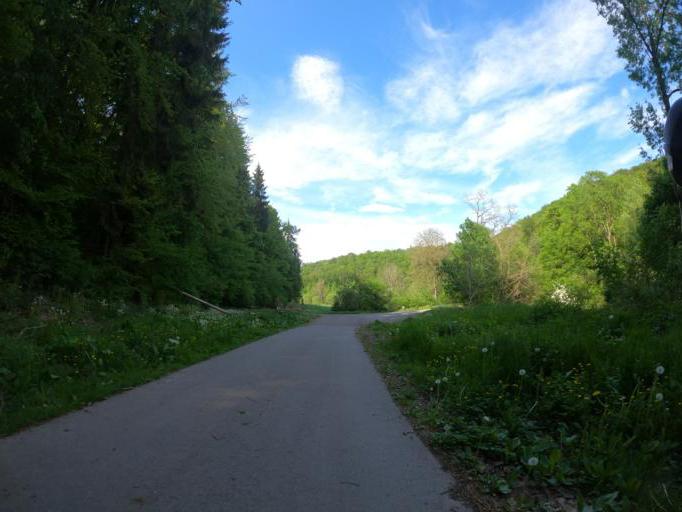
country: DE
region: Baden-Wuerttemberg
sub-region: Regierungsbezirk Stuttgart
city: Aidlingen
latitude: 48.6683
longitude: 8.9126
